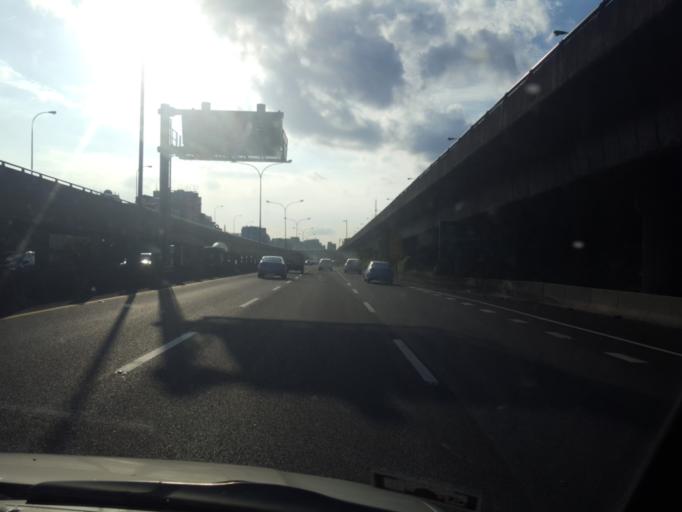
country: TW
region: Taipei
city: Taipei
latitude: 25.0645
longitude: 121.6041
